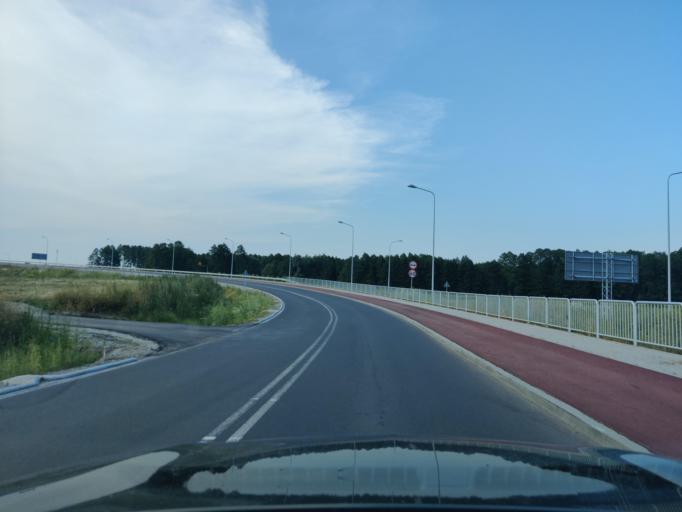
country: PL
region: Masovian Voivodeship
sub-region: Powiat mlawski
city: Strzegowo
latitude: 52.9310
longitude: 20.2882
